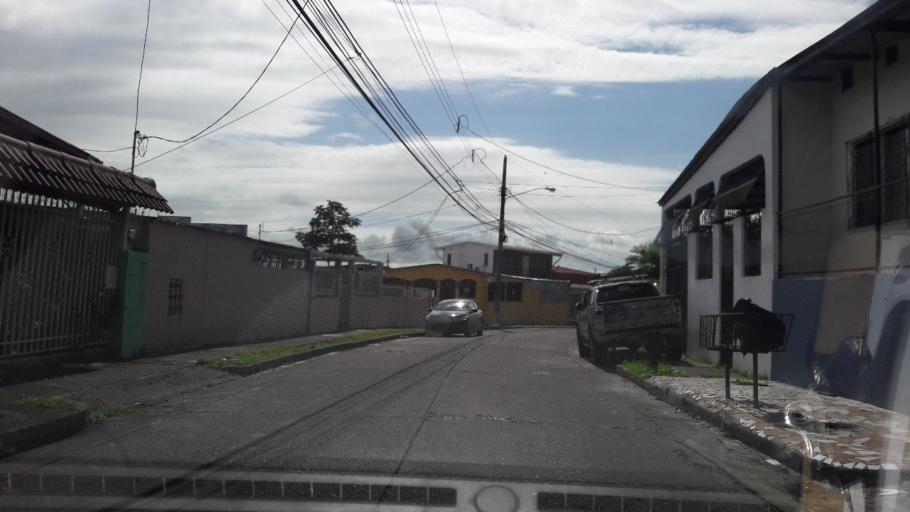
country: PA
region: Panama
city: Tocumen
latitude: 9.0608
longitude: -79.4163
